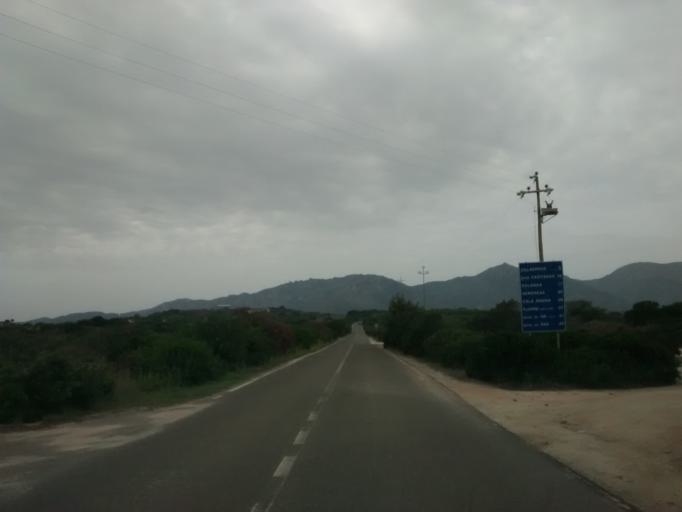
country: IT
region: Sardinia
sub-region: Provincia di Cagliari
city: Villasimius
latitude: 39.1076
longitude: 9.5152
